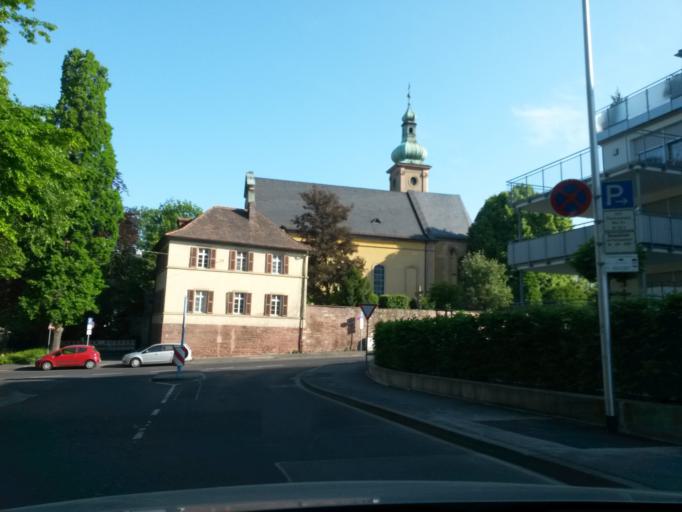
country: DE
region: Bavaria
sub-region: Regierungsbezirk Unterfranken
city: Bad Kissingen
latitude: 50.2005
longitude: 10.0834
